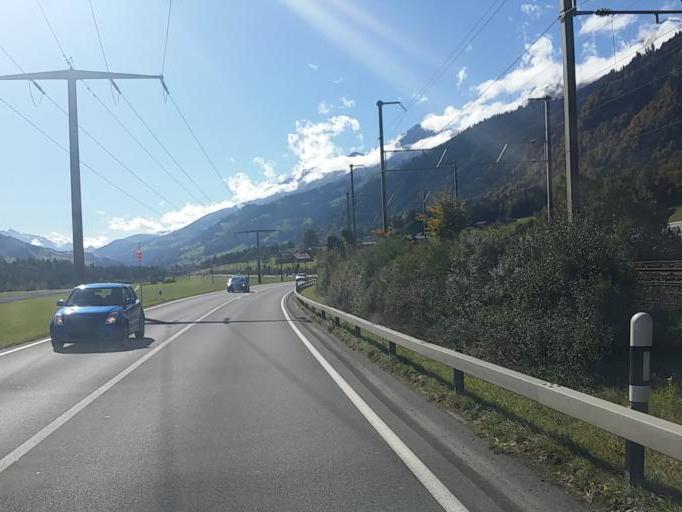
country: CH
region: Bern
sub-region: Frutigen-Niedersimmental District
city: Aeschi
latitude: 46.6173
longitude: 7.6808
